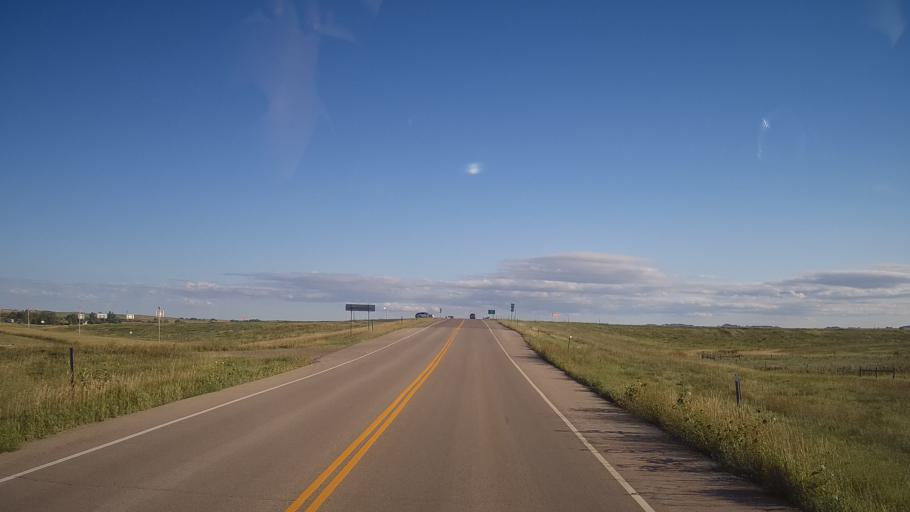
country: US
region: South Dakota
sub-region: Haakon County
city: Philip
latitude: 43.8436
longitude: -101.8997
